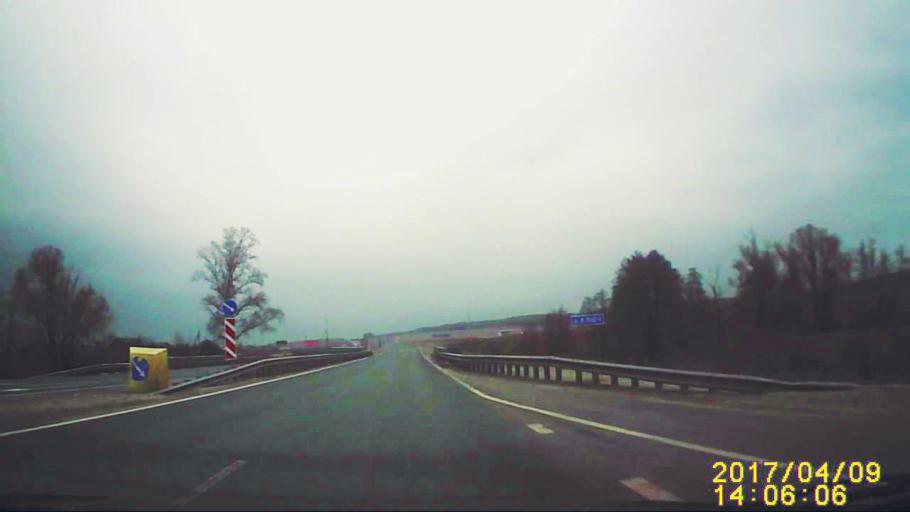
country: RU
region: Ulyanovsk
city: Silikatnyy
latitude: 54.0009
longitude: 48.2211
